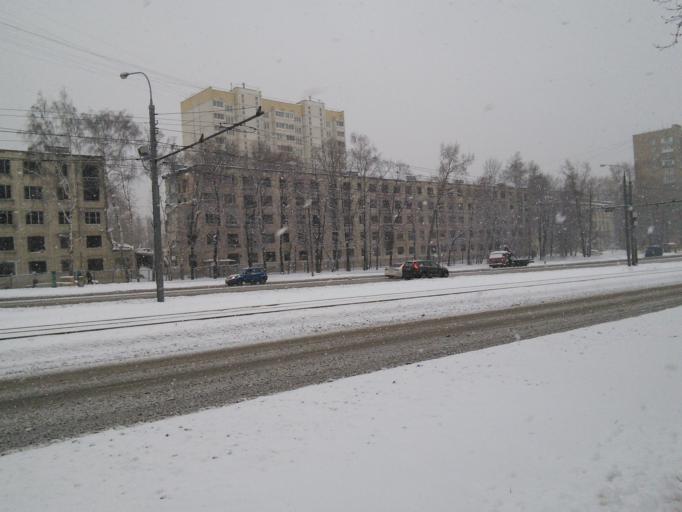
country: RU
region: Moscow
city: Kozeyevo
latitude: 55.8836
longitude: 37.6406
